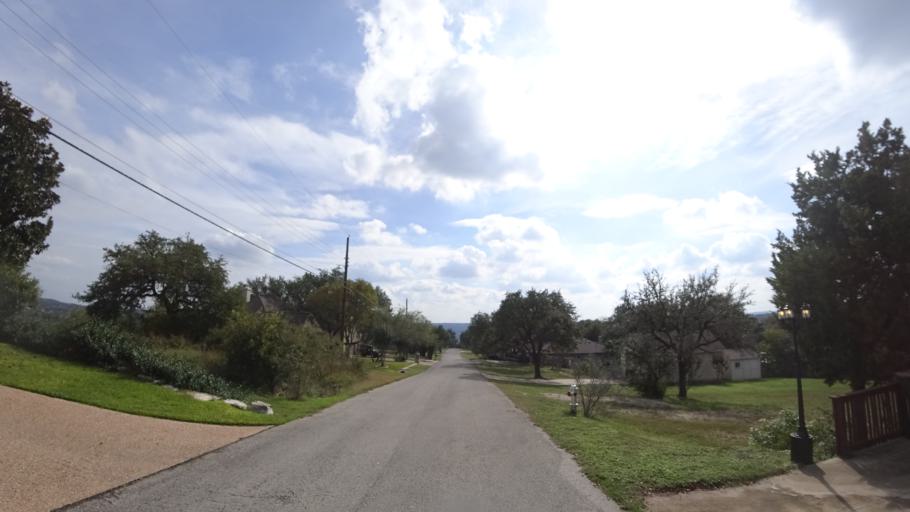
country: US
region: Texas
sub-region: Travis County
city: Hudson Bend
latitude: 30.3826
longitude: -97.9169
